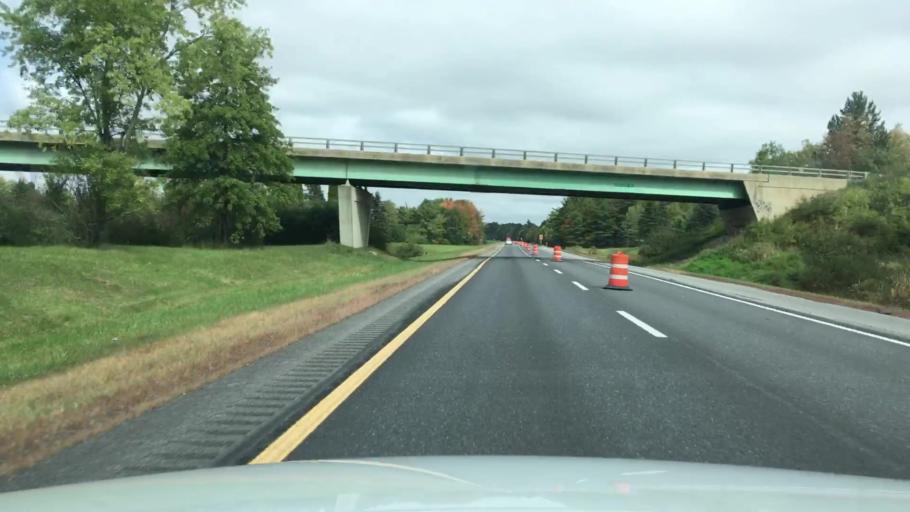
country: US
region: Maine
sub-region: Sagadahoc County
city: Richmond
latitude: 44.1132
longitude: -69.8578
